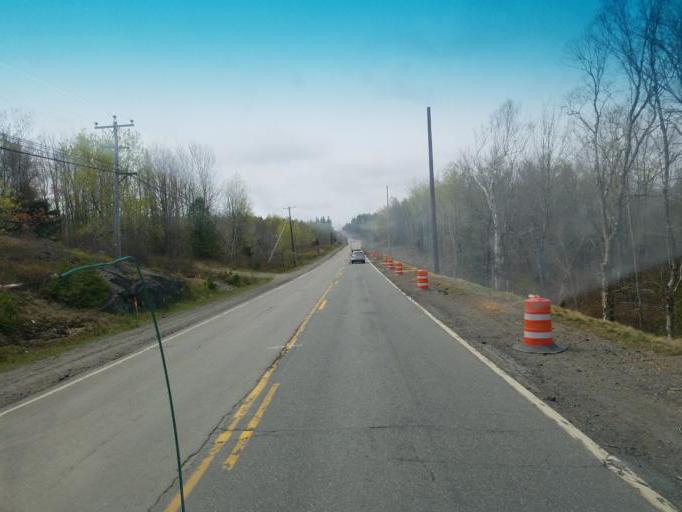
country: US
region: Maine
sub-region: Washington County
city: East Machias
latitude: 44.7790
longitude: -67.1953
